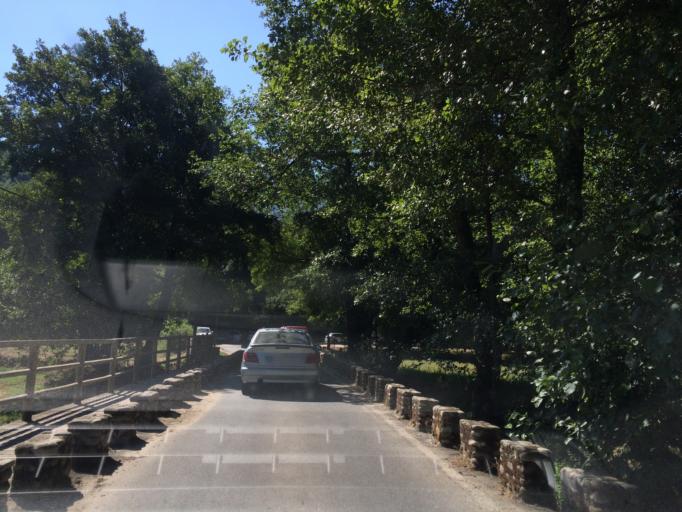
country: ES
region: Extremadura
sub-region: Provincia de Caceres
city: Jerte
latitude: 40.2085
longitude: -5.7723
